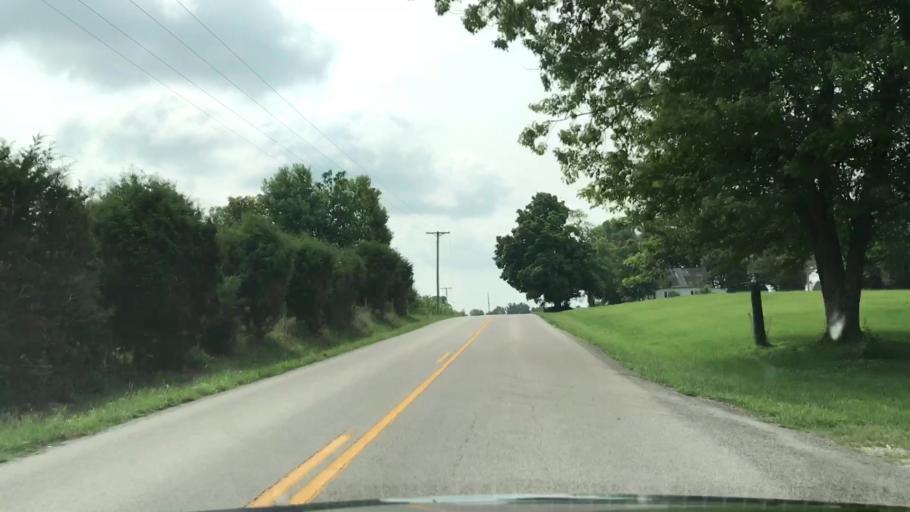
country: US
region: Kentucky
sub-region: Edmonson County
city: Brownsville
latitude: 37.1091
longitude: -86.1472
